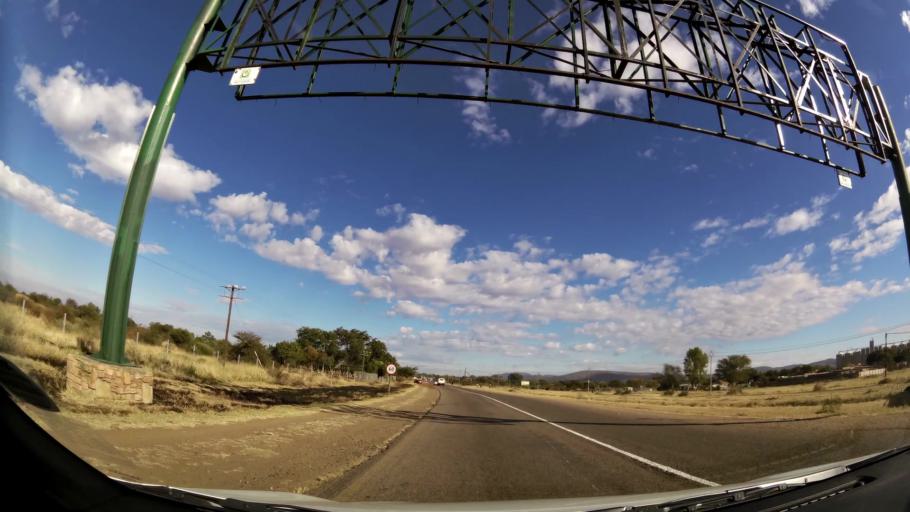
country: ZA
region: Limpopo
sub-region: Waterberg District Municipality
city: Bela-Bela
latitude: -24.8916
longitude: 28.3067
